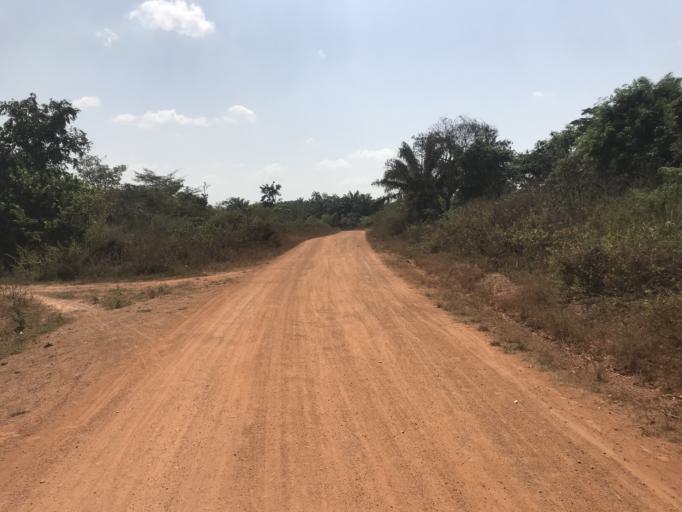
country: NG
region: Osun
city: Ifon
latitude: 7.9087
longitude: 4.4800
